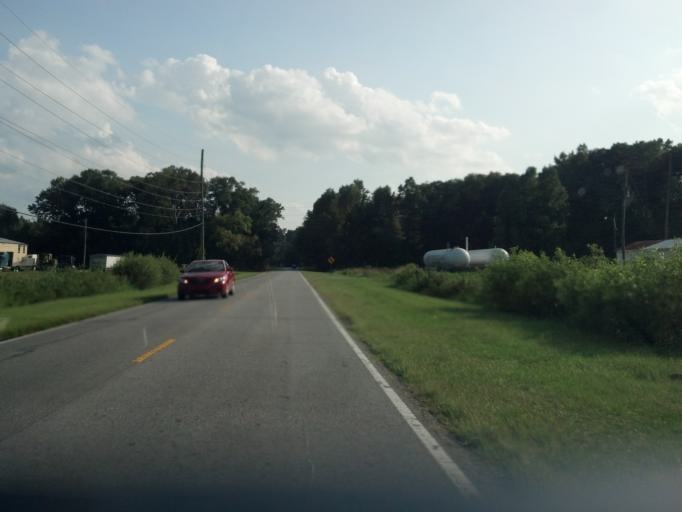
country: US
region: North Carolina
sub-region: Pitt County
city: Ayden
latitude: 35.4965
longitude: -77.4151
